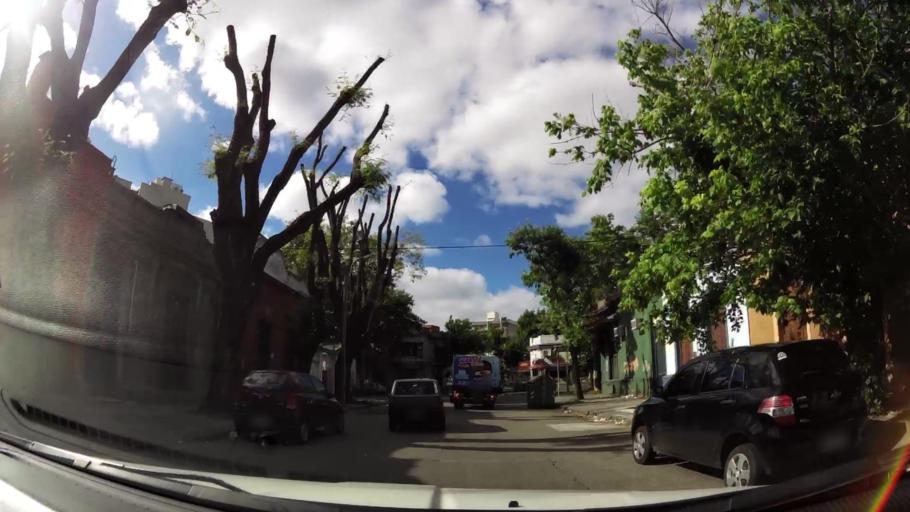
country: UY
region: Montevideo
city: Montevideo
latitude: -34.8768
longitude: -56.1773
